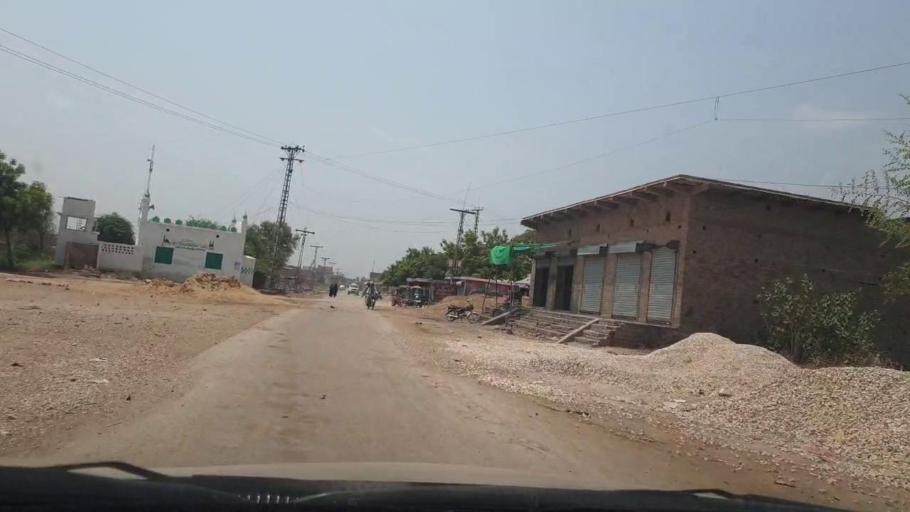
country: PK
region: Sindh
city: Ratodero
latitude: 27.7303
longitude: 68.2838
